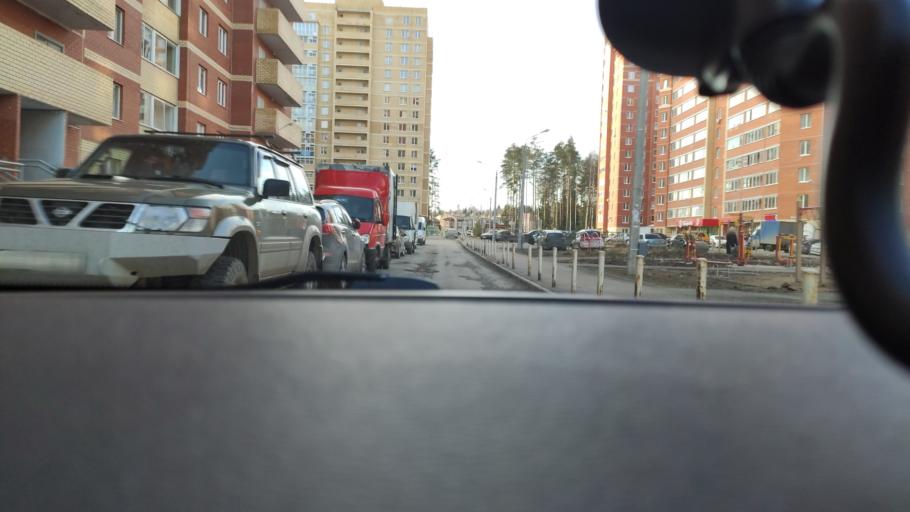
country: RU
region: Perm
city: Kondratovo
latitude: 58.0506
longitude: 56.0877
